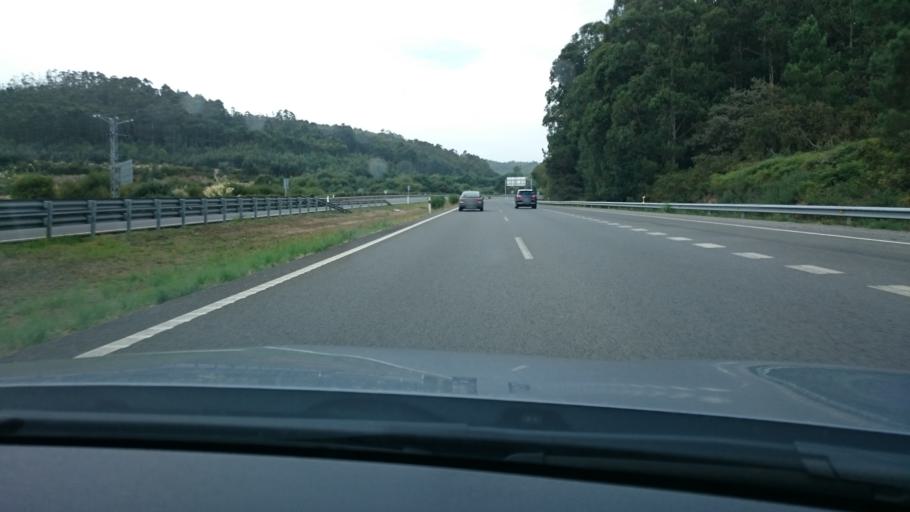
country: ES
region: Galicia
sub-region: Provincia da Coruna
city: Culleredo
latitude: 43.2762
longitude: -8.4110
